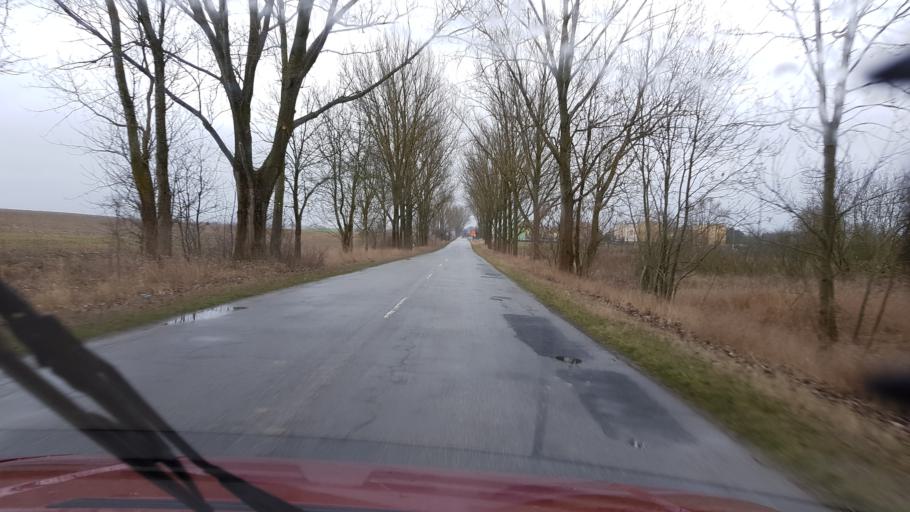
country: PL
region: West Pomeranian Voivodeship
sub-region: Powiat gryfinski
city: Gryfino
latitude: 53.2686
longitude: 14.6130
